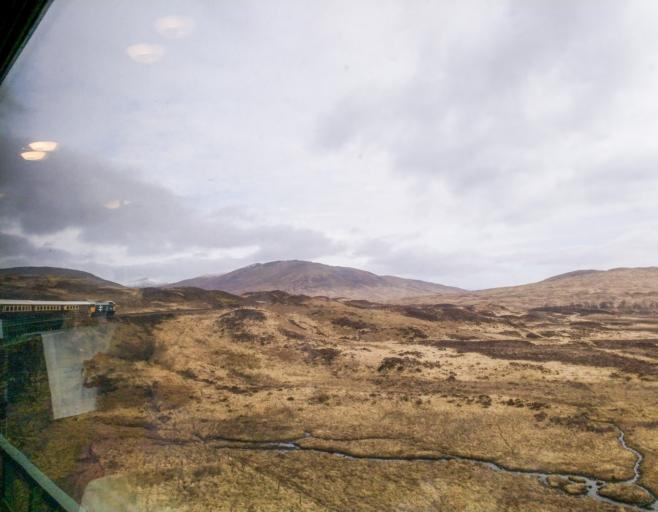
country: GB
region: Scotland
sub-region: Highland
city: Spean Bridge
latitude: 56.6897
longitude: -4.5768
